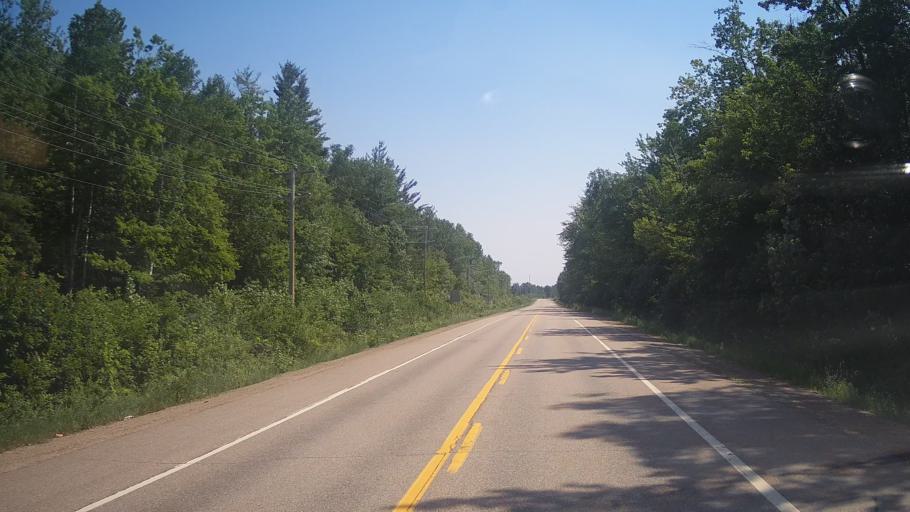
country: CA
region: Ontario
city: Pembroke
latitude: 45.8366
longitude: -77.0134
